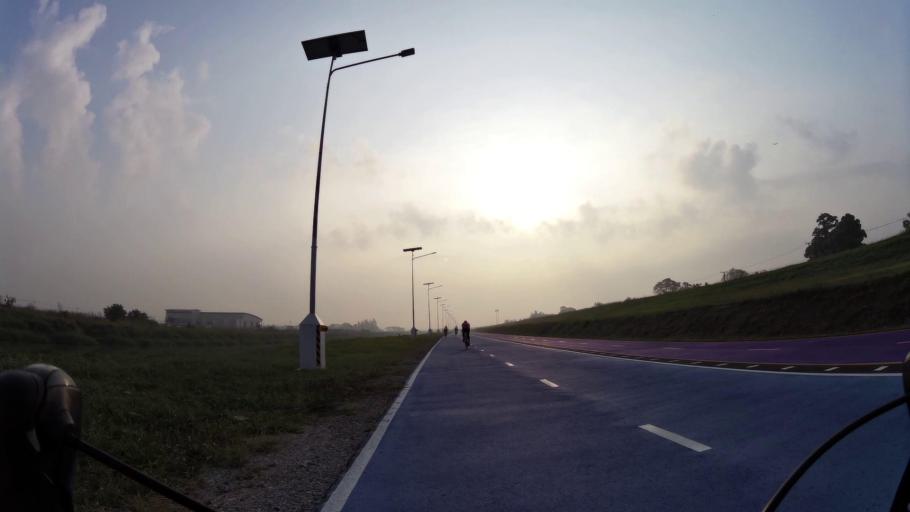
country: TH
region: Bangkok
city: Lat Krabang
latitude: 13.7058
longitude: 100.7816
